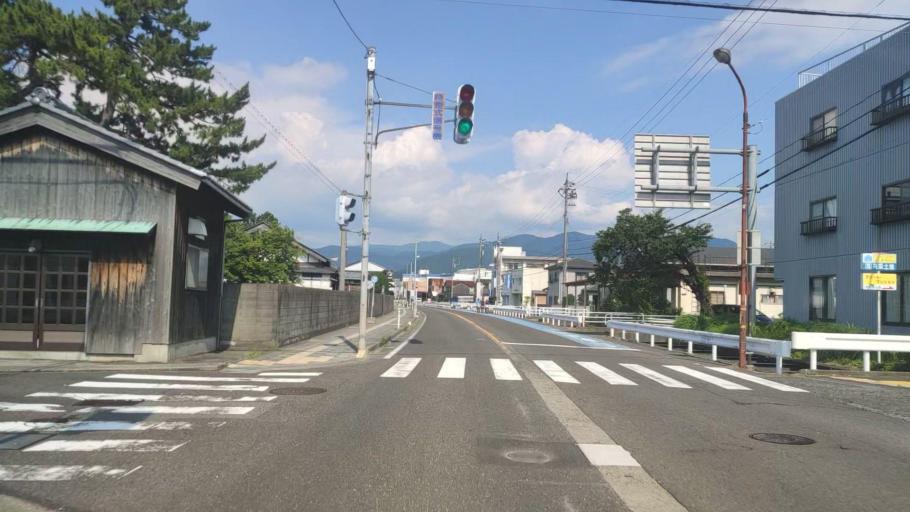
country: JP
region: Fukui
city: Tsuruga
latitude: 35.6522
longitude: 136.0562
